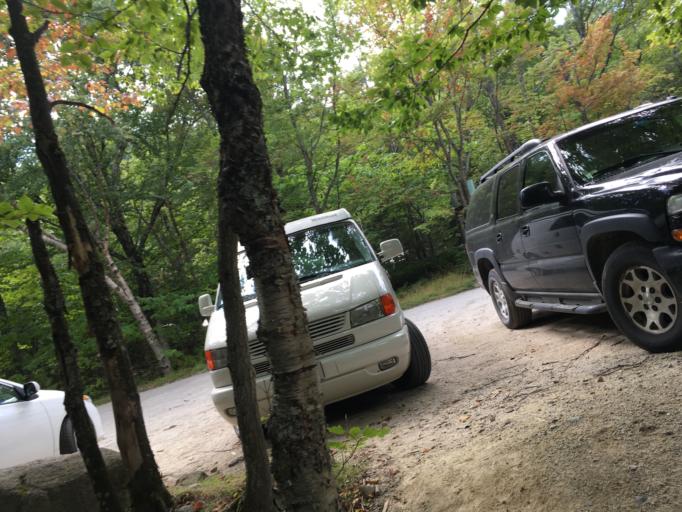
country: US
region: Maine
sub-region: Penobscot County
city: Millinocket
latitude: 45.9190
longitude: -68.8567
